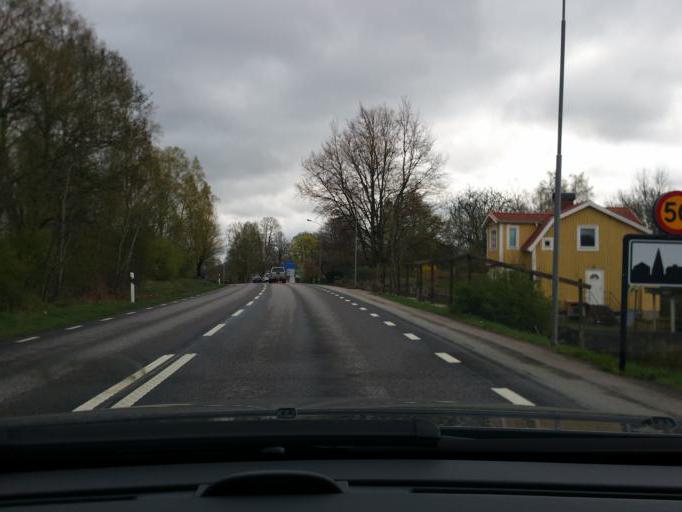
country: SE
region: Kronoberg
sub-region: Vaxjo Kommun
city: Ingelstad
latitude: 56.7430
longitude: 14.9274
